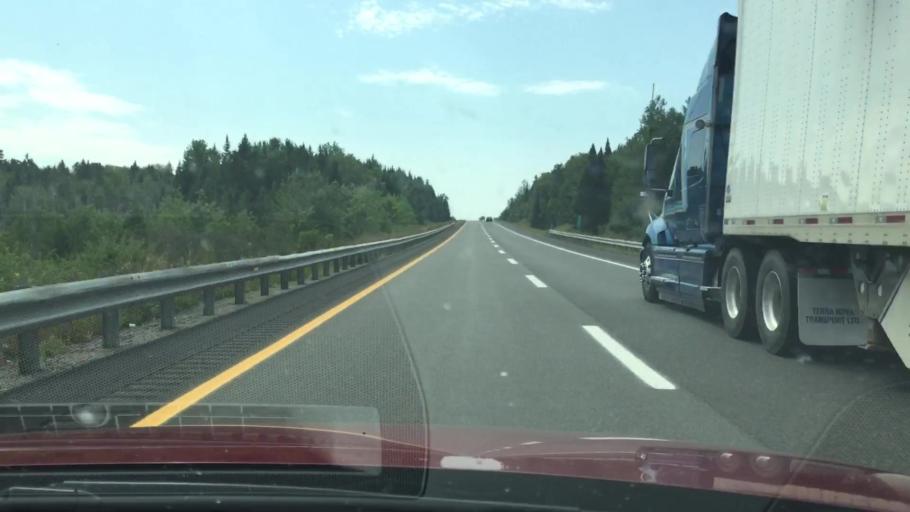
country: US
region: Maine
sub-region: Penobscot County
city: Patten
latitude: 46.0647
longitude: -68.2300
